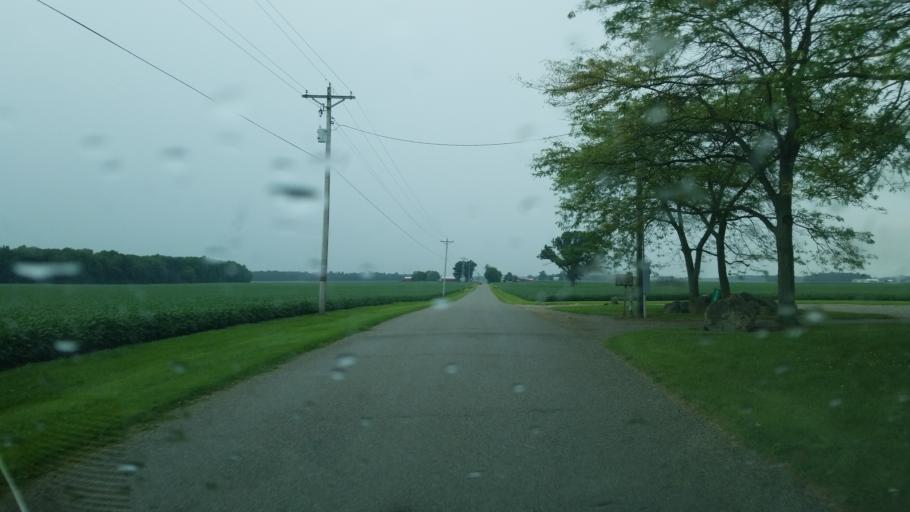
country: US
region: Ohio
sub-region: Huron County
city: Willard
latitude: 40.9971
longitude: -82.8136
